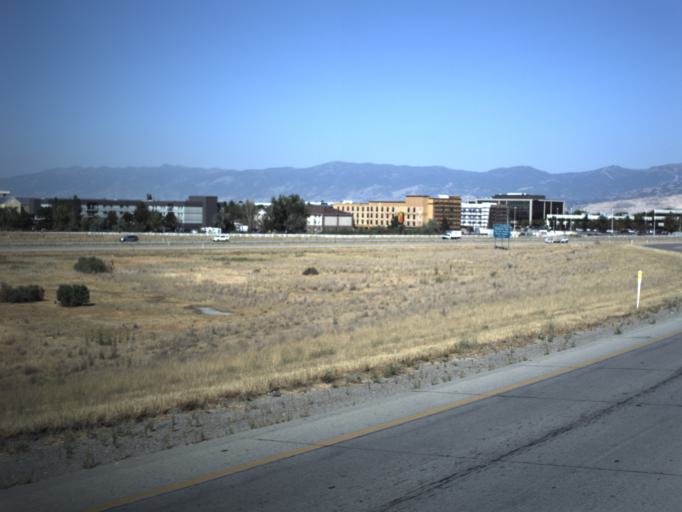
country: US
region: Utah
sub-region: Salt Lake County
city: West Valley City
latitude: 40.7692
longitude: -112.0235
